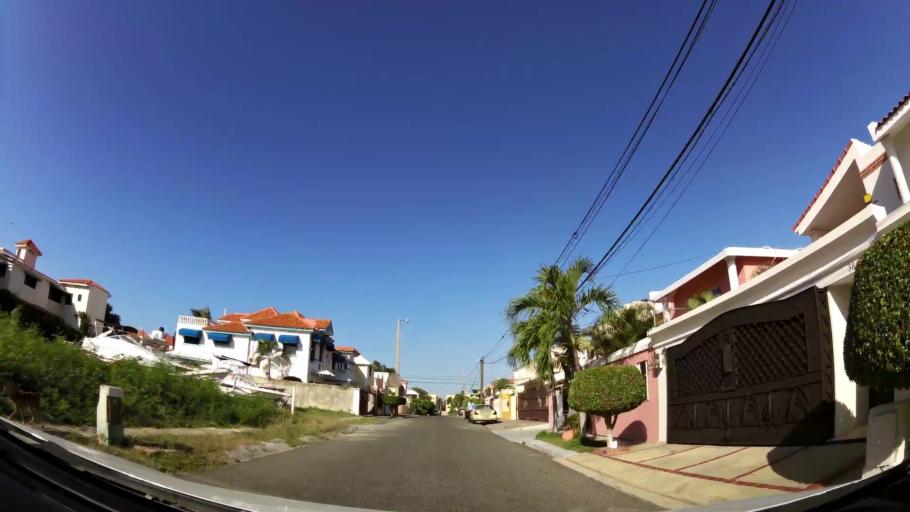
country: DO
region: Santo Domingo
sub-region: Santo Domingo
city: Santo Domingo Este
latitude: 18.4711
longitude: -69.8594
